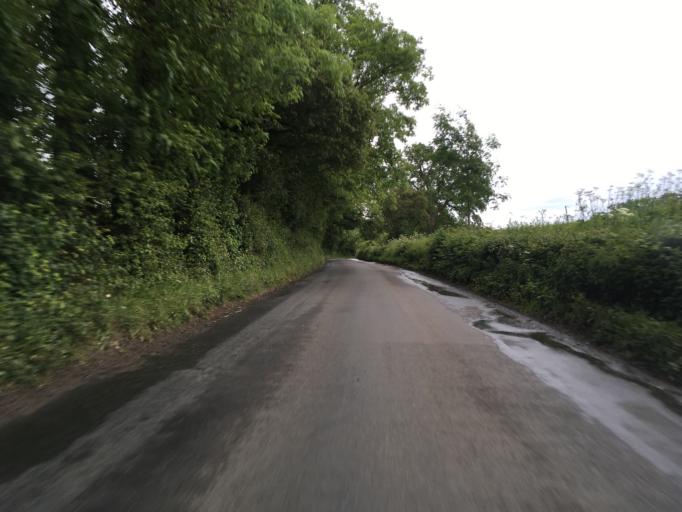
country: GB
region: England
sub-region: Gloucestershire
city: Tetbury
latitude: 51.6038
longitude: -2.1867
